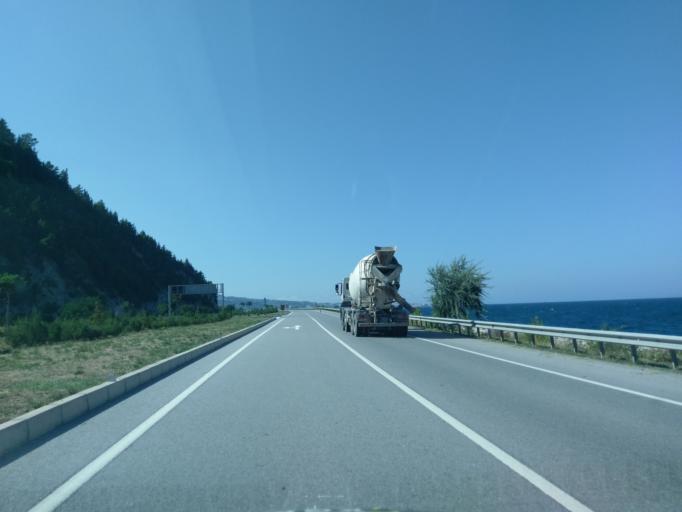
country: TR
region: Sinop
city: Gerze
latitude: 41.7482
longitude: 35.2422
